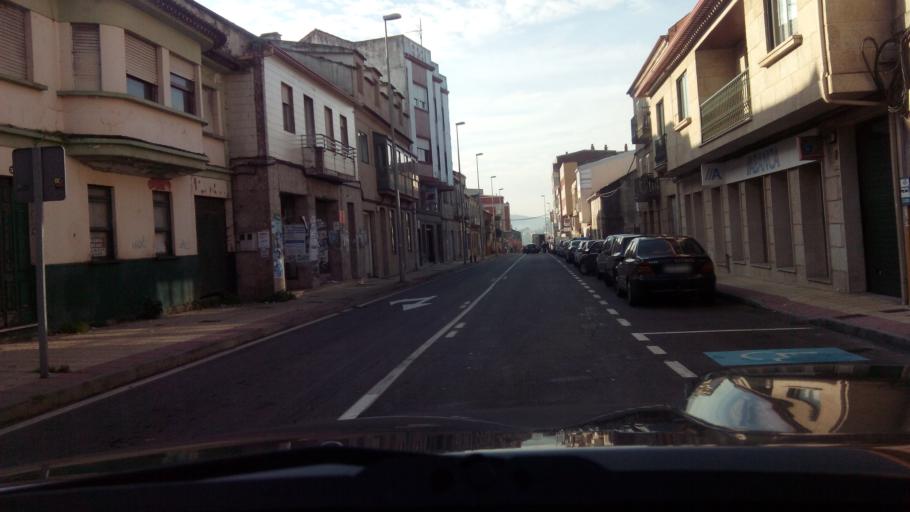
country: ES
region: Galicia
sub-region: Provincia de Pontevedra
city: Marin
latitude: 42.3703
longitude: -8.7309
